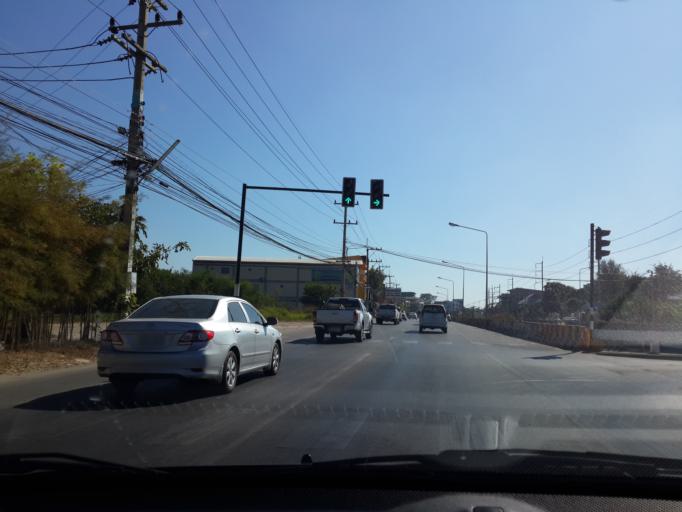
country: TH
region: Chiang Mai
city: Chiang Mai
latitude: 18.7837
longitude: 98.9584
